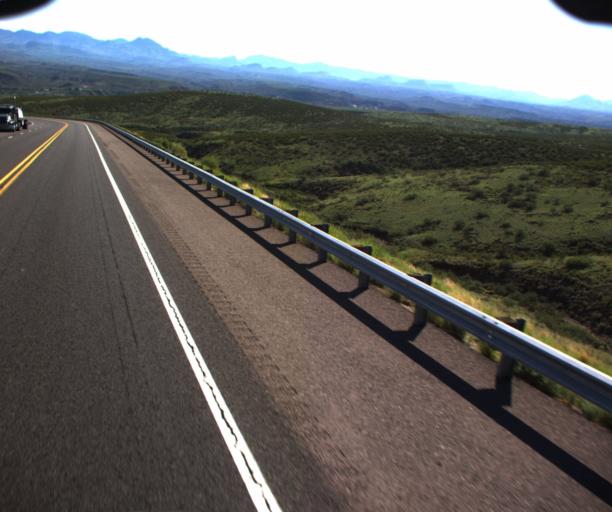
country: US
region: Arizona
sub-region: Greenlee County
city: Clifton
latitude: 32.9256
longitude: -109.2420
